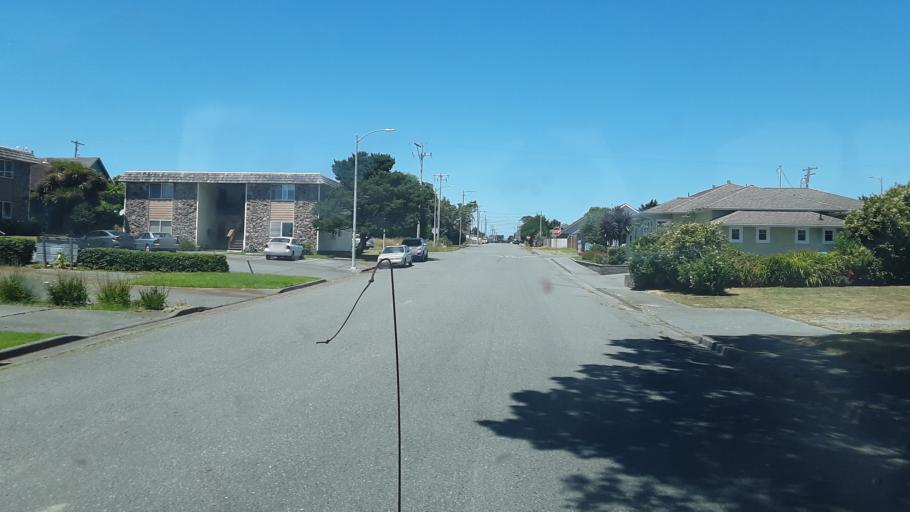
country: US
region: California
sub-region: Del Norte County
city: Crescent City
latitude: 41.7488
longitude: -124.2027
